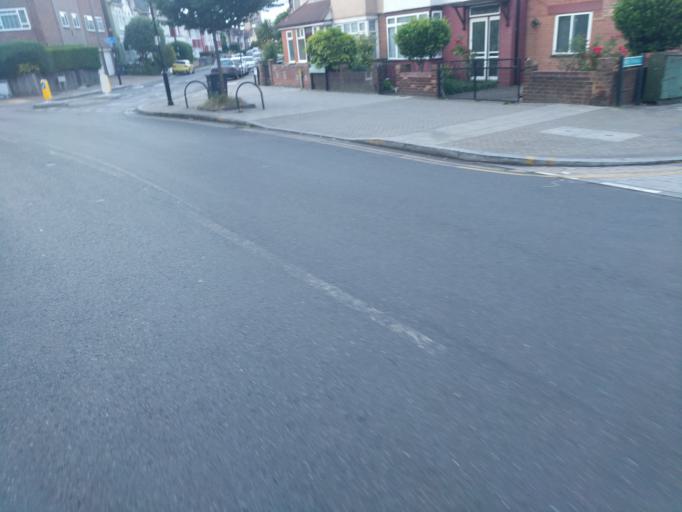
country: GB
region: England
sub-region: Greater London
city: Catford
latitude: 51.4570
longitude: -0.0200
